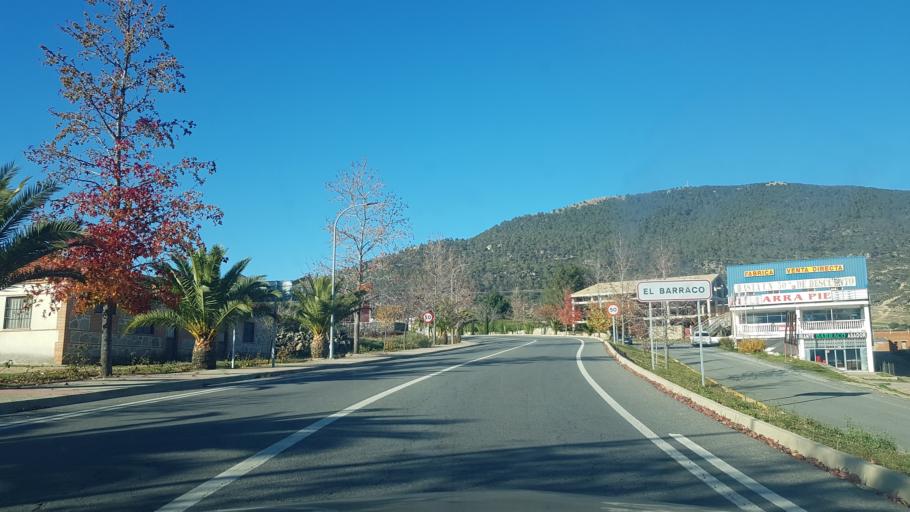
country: ES
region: Castille and Leon
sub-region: Provincia de Avila
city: Barraco
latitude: 40.4728
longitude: -4.6362
